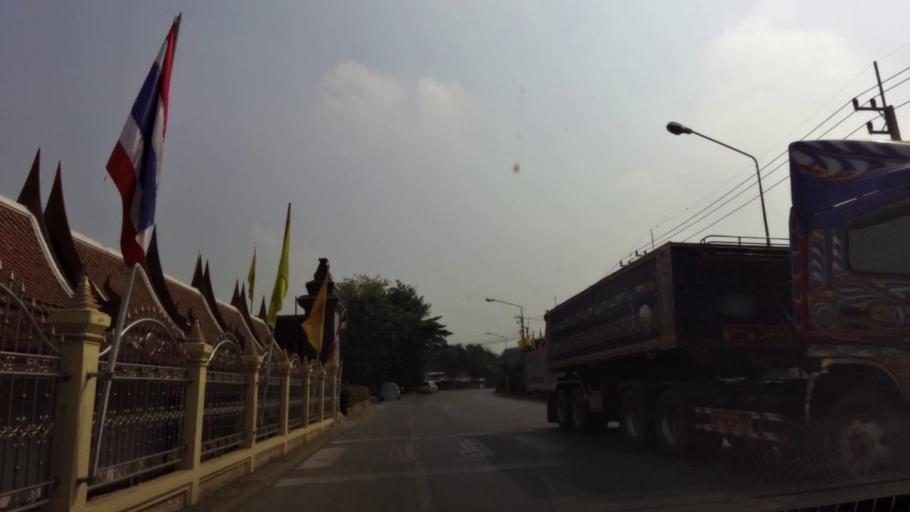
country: TH
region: Phra Nakhon Si Ayutthaya
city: Phra Nakhon Si Ayutthaya
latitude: 14.3433
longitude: 100.5799
